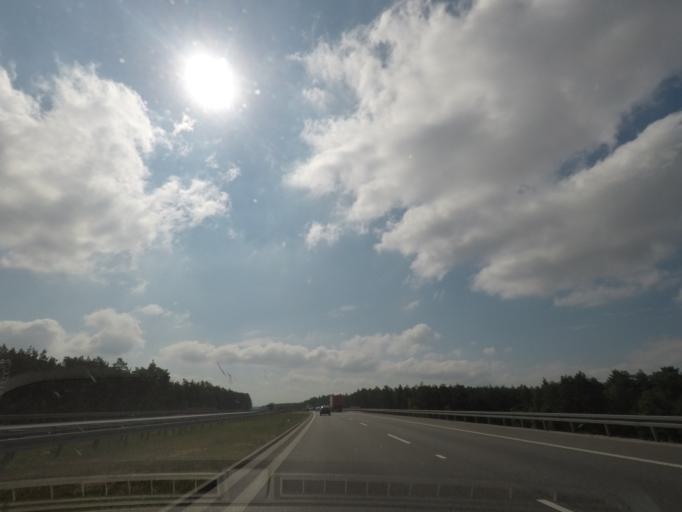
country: PL
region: Kujawsko-Pomorskie
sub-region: Powiat aleksandrowski
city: Aleksandrow Kujawski
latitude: 52.8939
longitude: 18.7265
